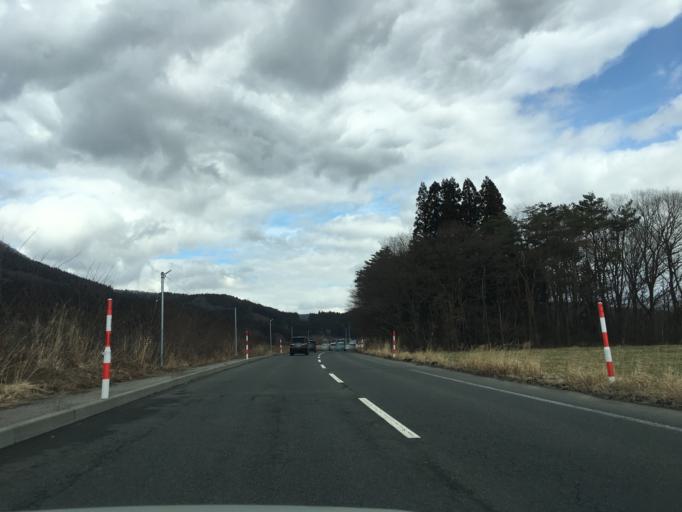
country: JP
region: Akita
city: Hanawa
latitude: 40.2301
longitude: 140.6817
